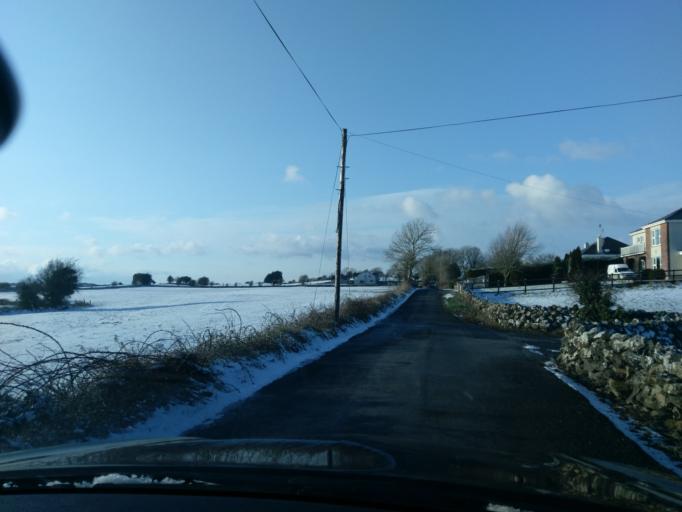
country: IE
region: Connaught
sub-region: County Galway
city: Athenry
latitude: 53.1920
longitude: -8.7319
